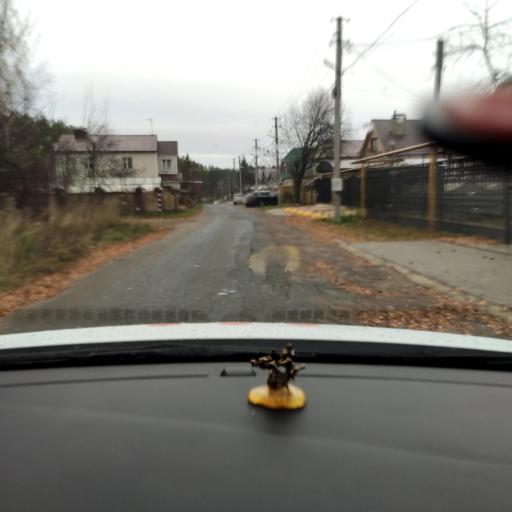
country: RU
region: Tatarstan
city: Vysokaya Gora
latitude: 55.8466
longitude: 49.2385
